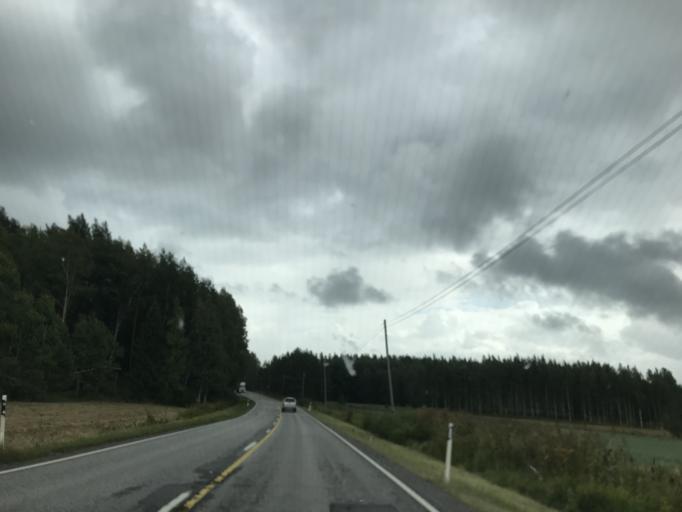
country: FI
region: Varsinais-Suomi
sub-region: Salo
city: Pernioe
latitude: 60.0859
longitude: 23.2306
